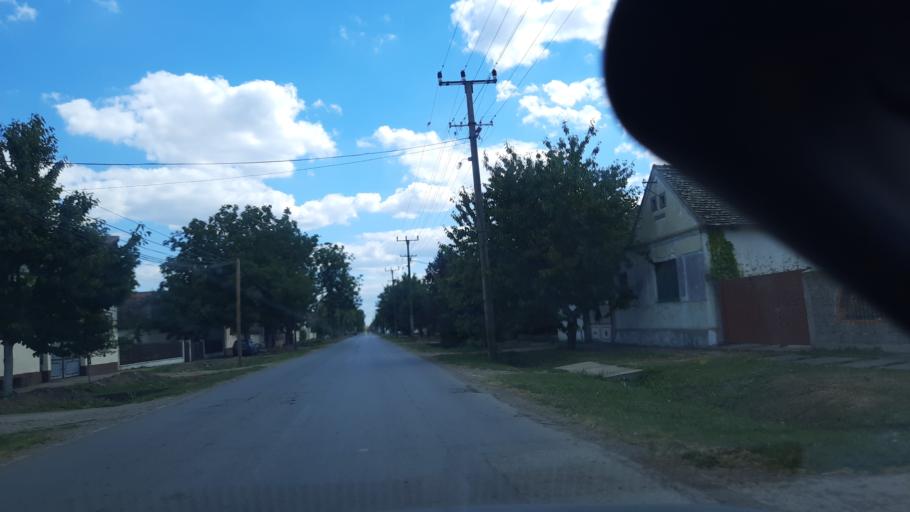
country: RS
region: Autonomna Pokrajina Vojvodina
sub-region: Sremski Okrug
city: Pecinci
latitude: 44.9317
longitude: 20.0071
